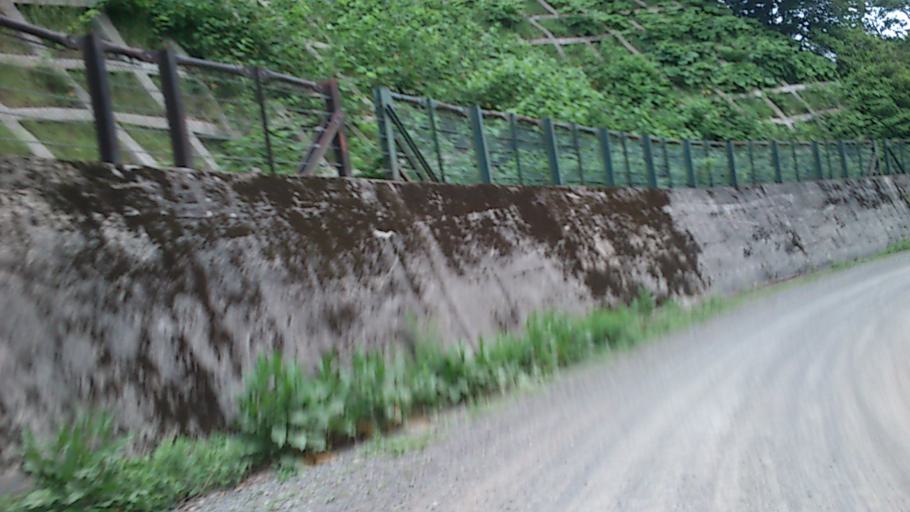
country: JP
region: Aomori
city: Hirosaki
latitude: 40.5427
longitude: 140.1809
